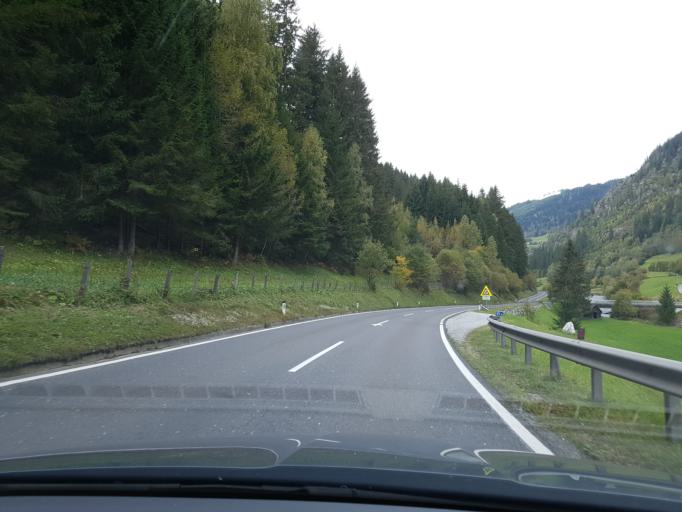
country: AT
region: Salzburg
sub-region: Politischer Bezirk Tamsweg
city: Ramingstein
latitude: 47.0708
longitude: 13.8677
